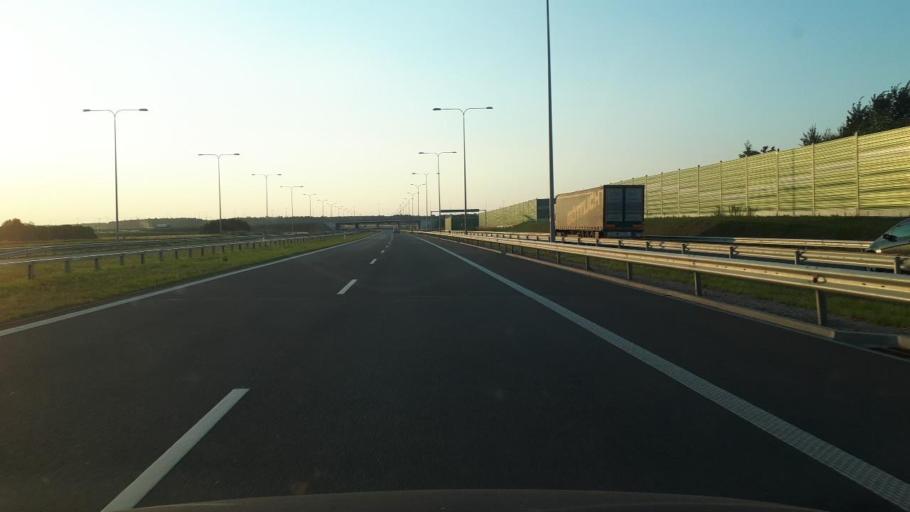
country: PL
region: Greater Poland Voivodeship
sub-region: Powiat kepinski
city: Kepno
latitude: 51.3109
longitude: 18.0138
